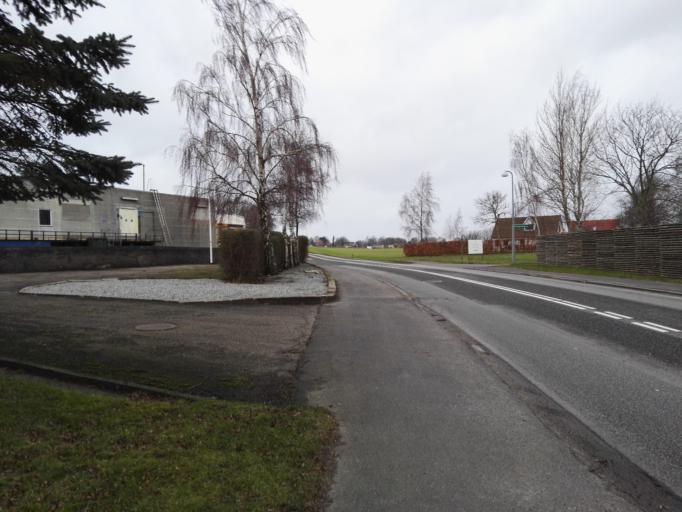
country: DK
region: Zealand
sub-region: Lejre Kommune
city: Ejby
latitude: 55.6865
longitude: 11.9181
